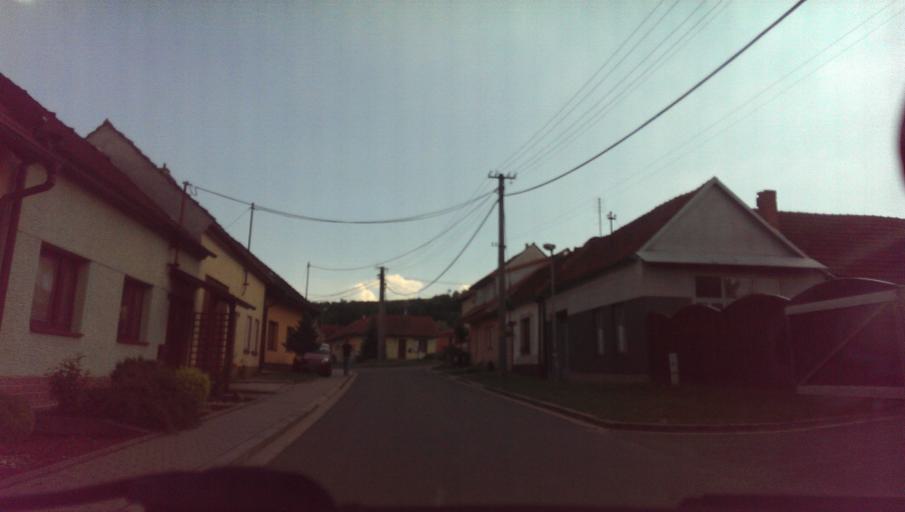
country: CZ
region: Zlin
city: Popovice
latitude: 49.0372
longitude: 17.5044
